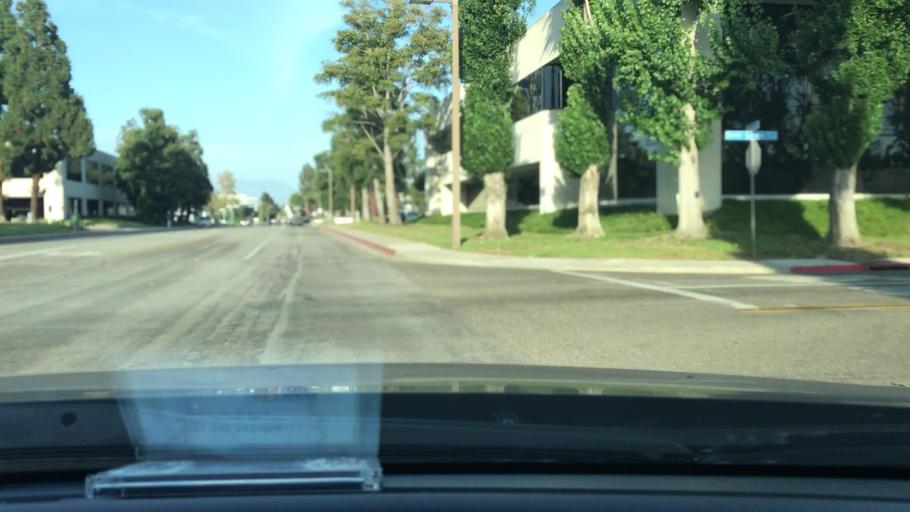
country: US
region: California
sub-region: Orange County
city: Fountain Valley
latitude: 33.6991
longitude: -117.9228
